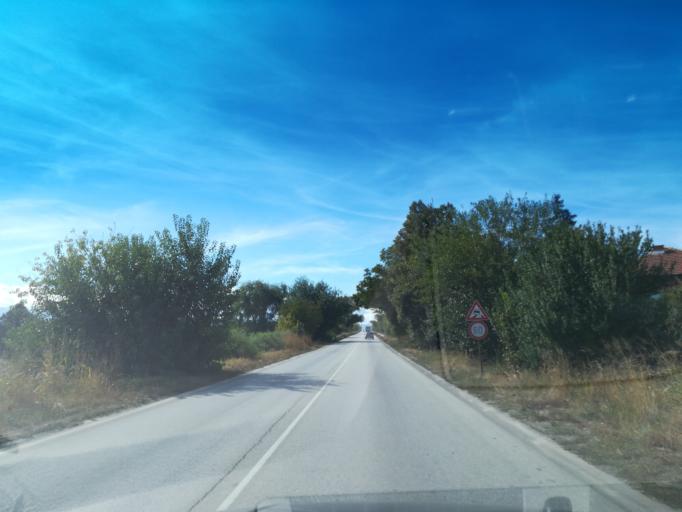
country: BG
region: Plovdiv
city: Stamboliyski
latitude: 42.1330
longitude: 24.6099
